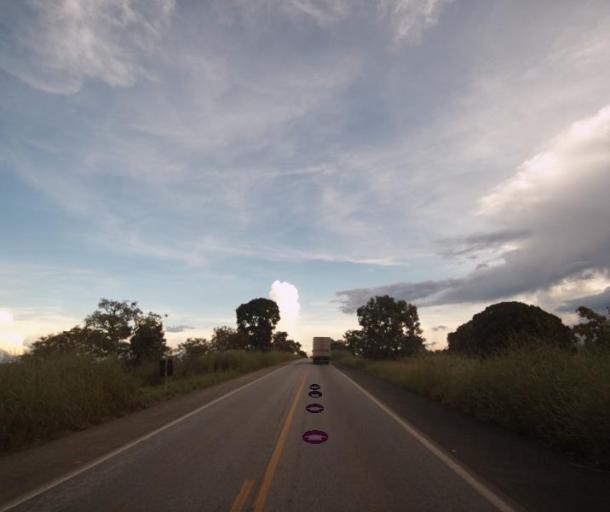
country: BR
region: Goias
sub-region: Uruacu
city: Uruacu
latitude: -14.2473
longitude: -49.1387
